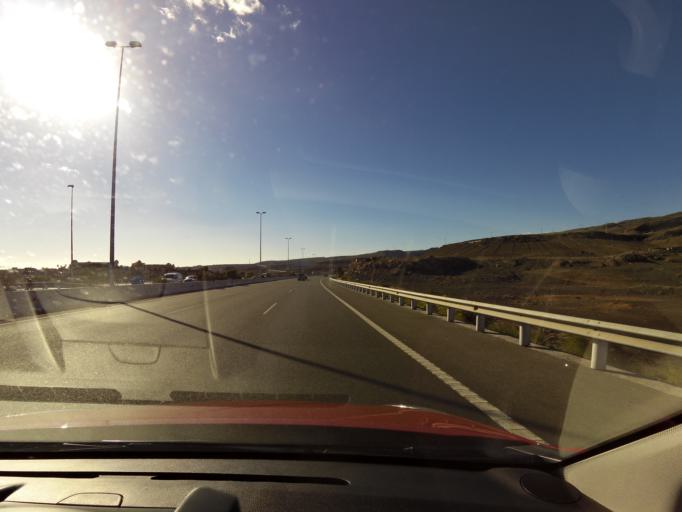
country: ES
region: Canary Islands
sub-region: Provincia de Las Palmas
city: Playa del Ingles
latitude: 27.7874
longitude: -15.5094
